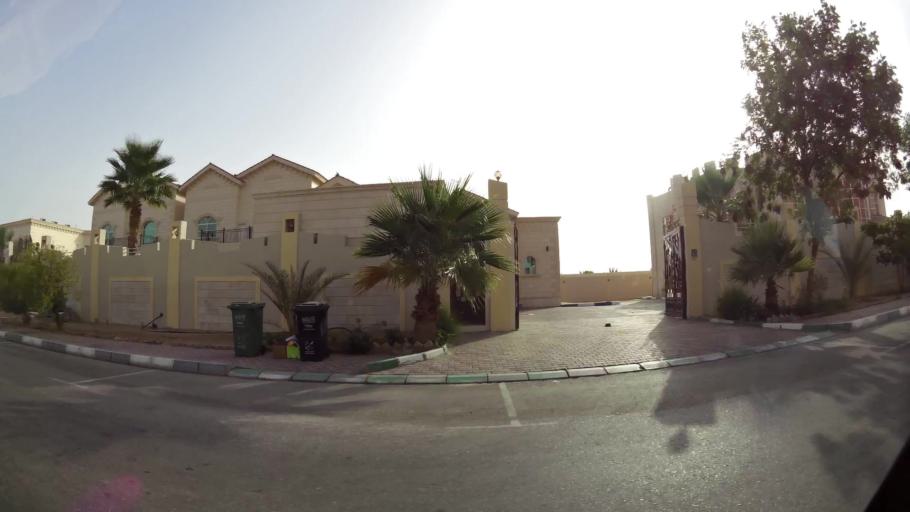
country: AE
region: Abu Dhabi
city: Al Ain
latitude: 24.1251
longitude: 55.6947
